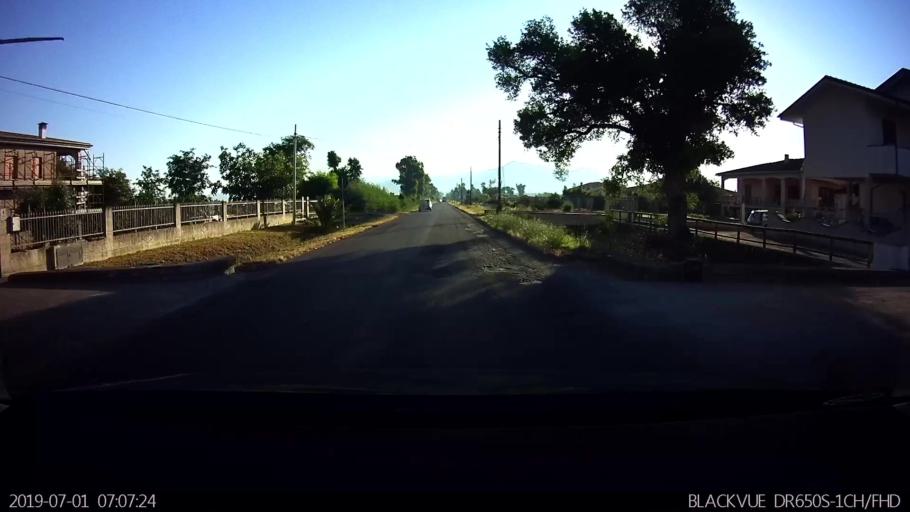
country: IT
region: Latium
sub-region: Provincia di Latina
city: Borgo Hermada
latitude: 41.2887
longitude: 13.1386
